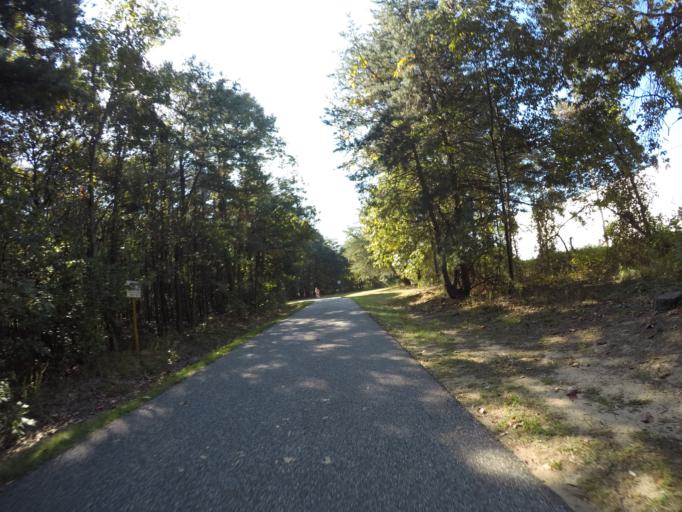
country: US
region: Maryland
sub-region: Anne Arundel County
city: Ferndale
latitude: 39.1580
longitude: -76.6607
